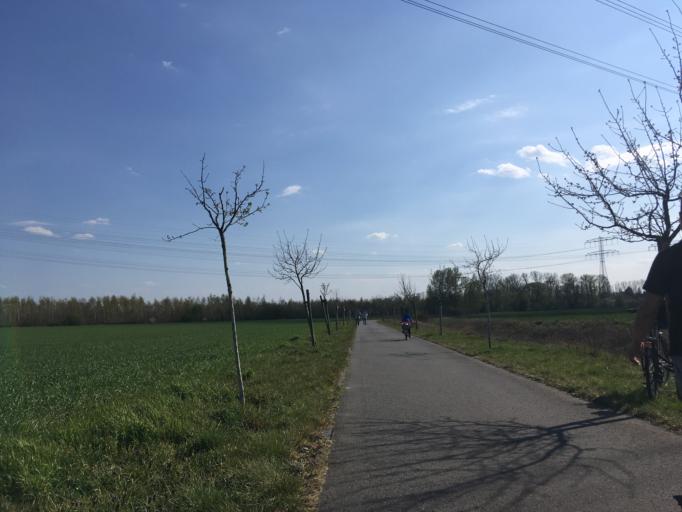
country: DE
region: Berlin
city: Wartenberg
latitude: 52.5923
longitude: 13.5004
